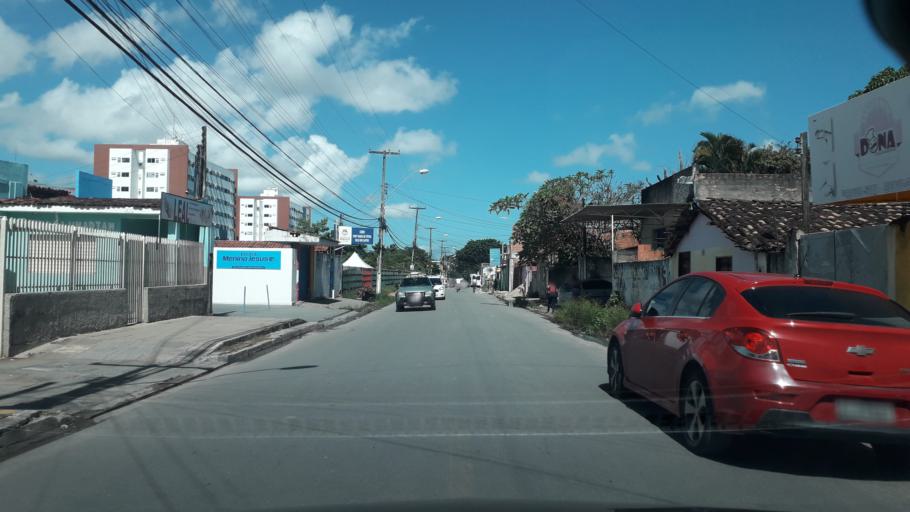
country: BR
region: Alagoas
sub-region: Satuba
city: Satuba
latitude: -9.5789
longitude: -35.7709
